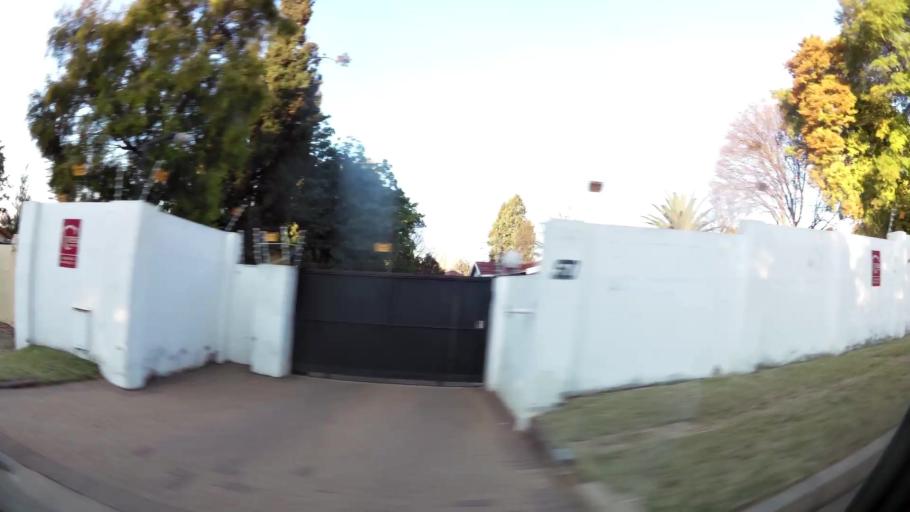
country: ZA
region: Gauteng
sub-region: City of Johannesburg Metropolitan Municipality
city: Diepsloot
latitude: -26.0492
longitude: 27.9770
